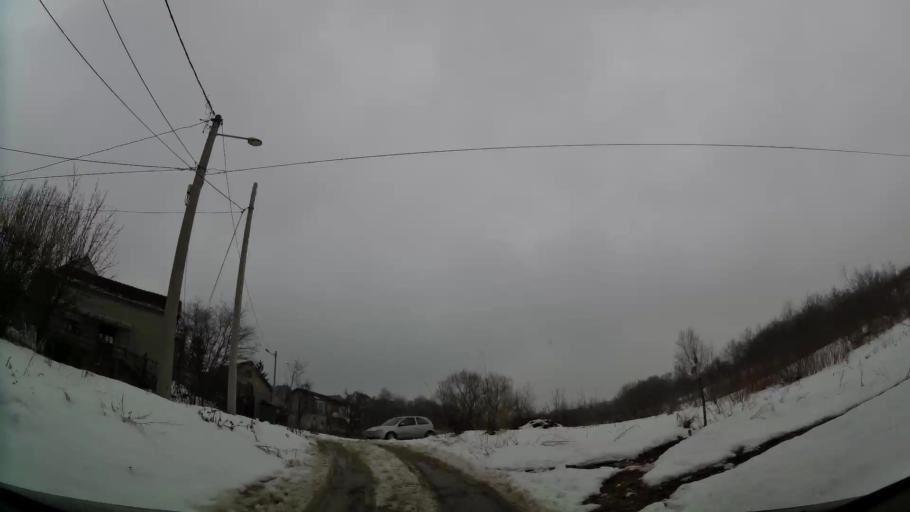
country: RS
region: Central Serbia
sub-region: Belgrade
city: Zvezdara
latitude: 44.7514
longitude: 20.5244
